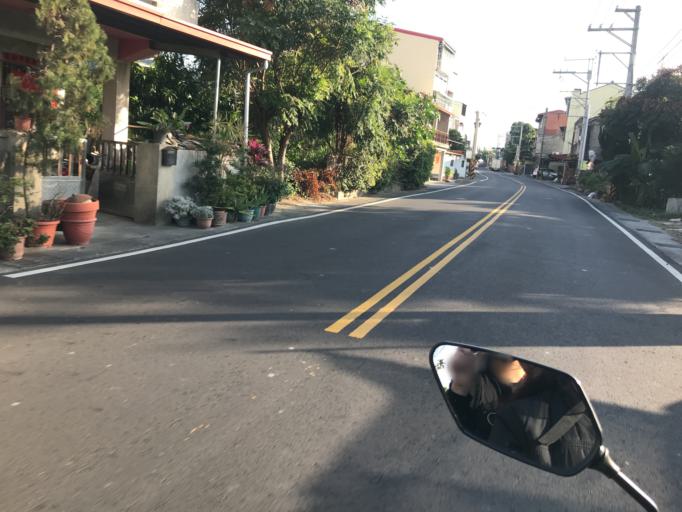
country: TW
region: Taiwan
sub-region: Nantou
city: Nantou
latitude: 23.8655
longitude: 120.6029
